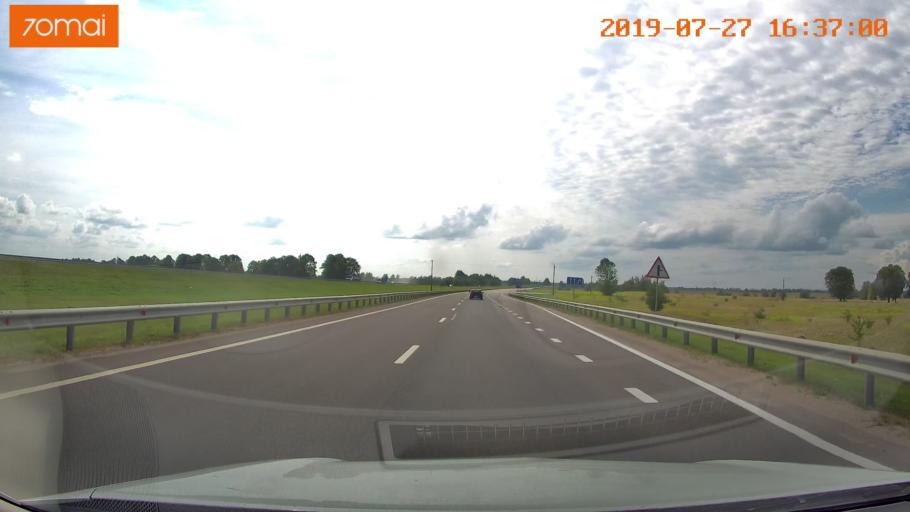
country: RU
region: Kaliningrad
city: Gvardeysk
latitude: 54.6486
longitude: 21.2677
